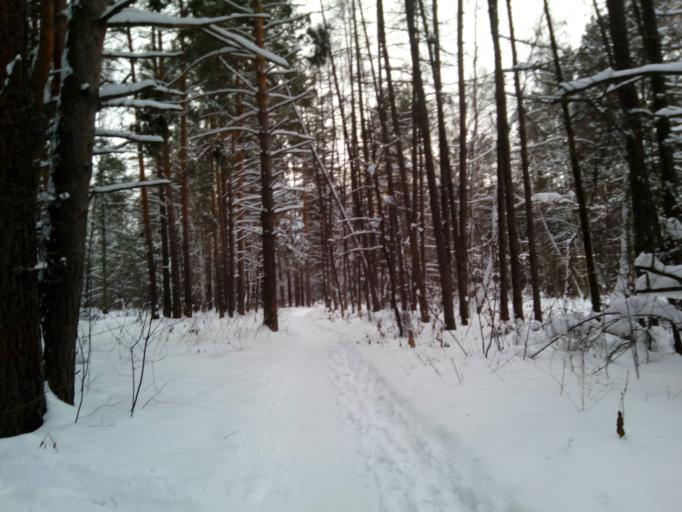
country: RU
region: Novosibirsk
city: Akademgorodok
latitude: 54.8573
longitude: 83.0928
